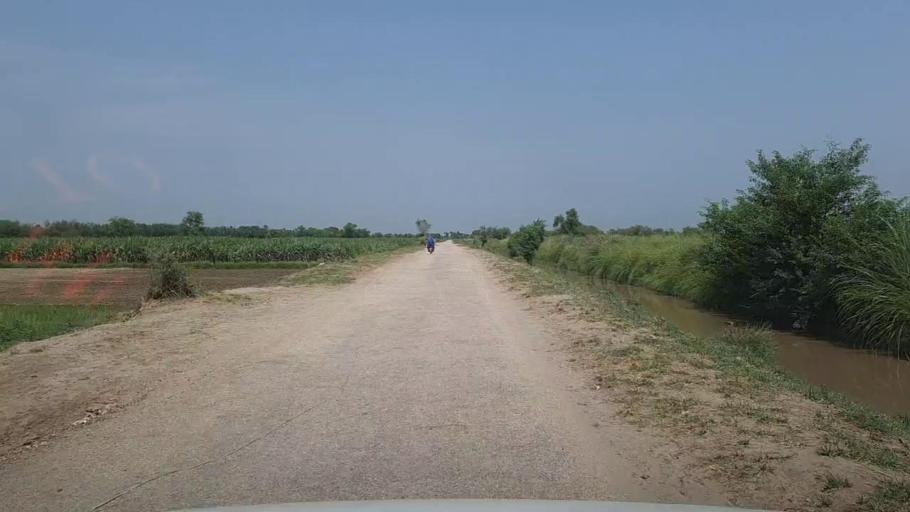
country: PK
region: Sindh
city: Karaundi
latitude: 26.8809
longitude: 68.3351
